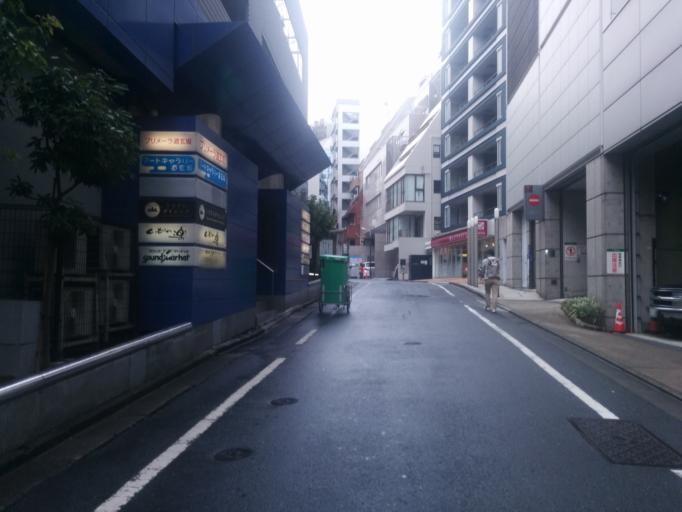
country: JP
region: Tokyo
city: Tokyo
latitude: 35.6576
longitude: 139.6977
